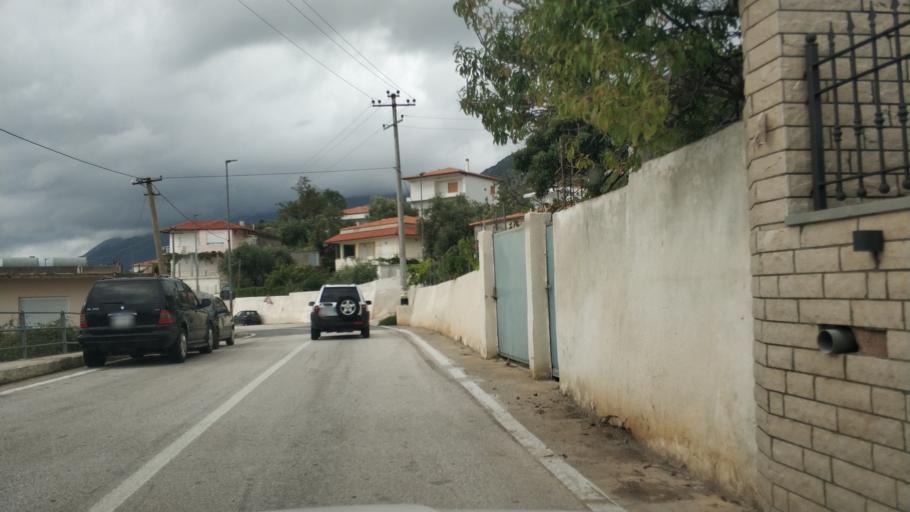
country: AL
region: Vlore
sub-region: Rrethi i Vlores
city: Vranisht
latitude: 40.1508
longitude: 19.6403
